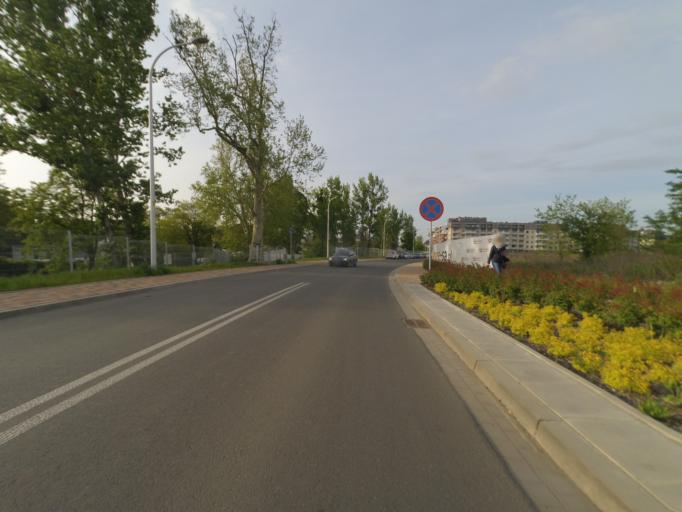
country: PL
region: Lower Silesian Voivodeship
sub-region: Powiat wroclawski
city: Wroclaw
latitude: 51.1265
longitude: 17.0388
